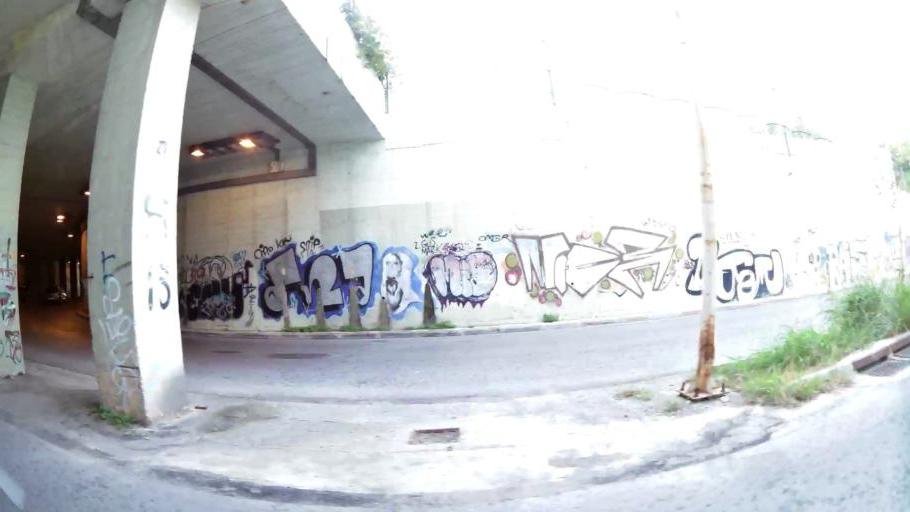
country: GR
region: Attica
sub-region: Nomarchia Athinas
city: Chaidari
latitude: 38.0166
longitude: 23.6692
